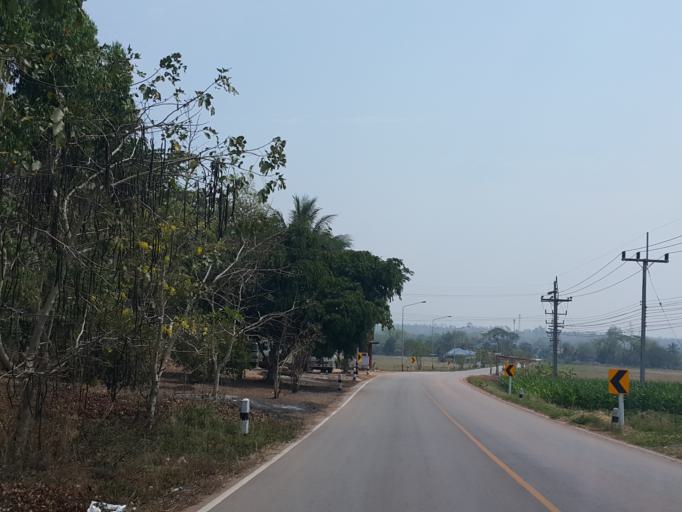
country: TH
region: Lampang
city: Chae Hom
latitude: 18.7613
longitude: 99.5567
